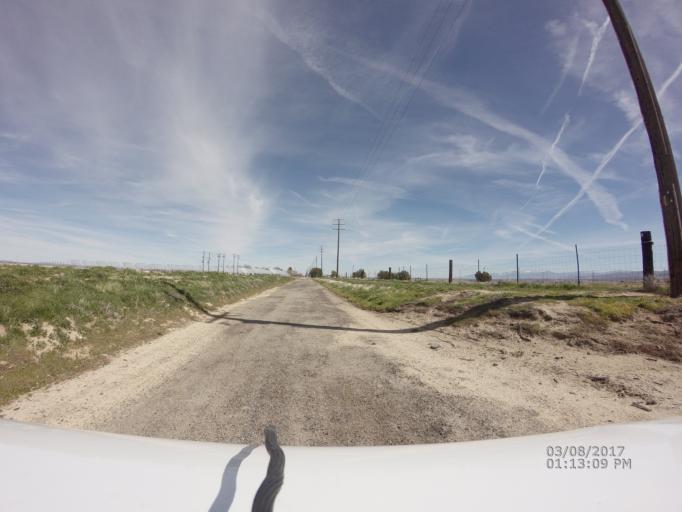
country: US
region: California
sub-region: Los Angeles County
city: Leona Valley
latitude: 34.7184
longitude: -118.2960
